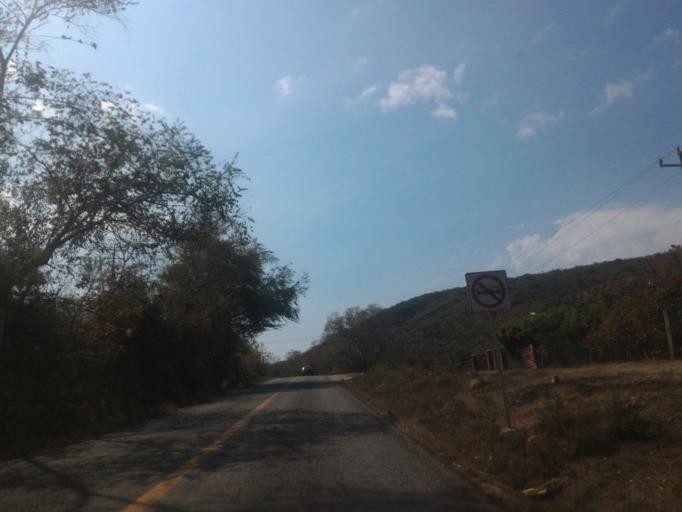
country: MX
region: Michoacan
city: Coahuayana Viejo
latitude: 18.4602
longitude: -103.5414
